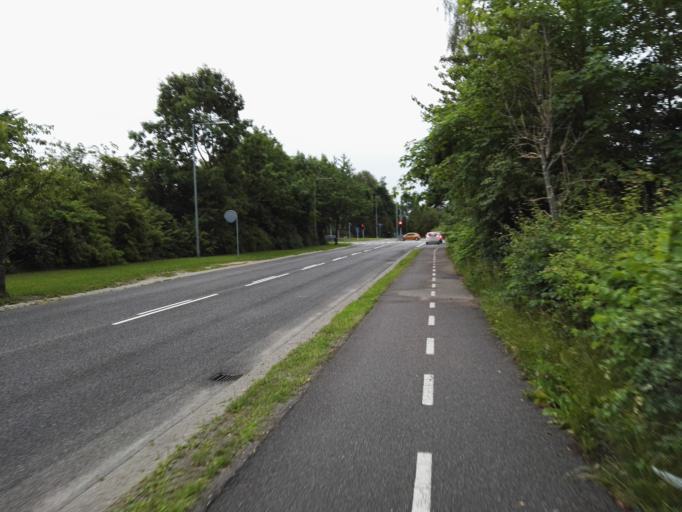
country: DK
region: Capital Region
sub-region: Egedal Kommune
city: Smorumnedre
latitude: 55.7403
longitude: 12.3147
